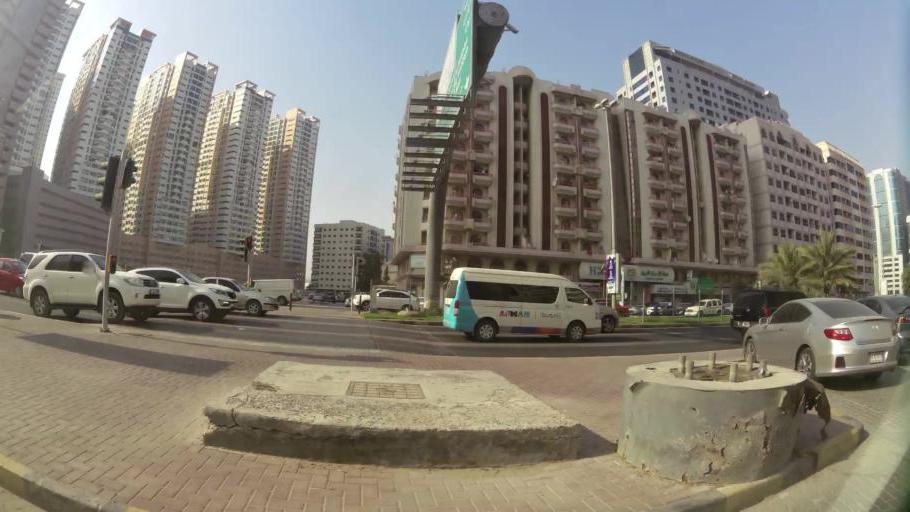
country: AE
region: Ajman
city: Ajman
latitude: 25.3927
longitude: 55.4322
